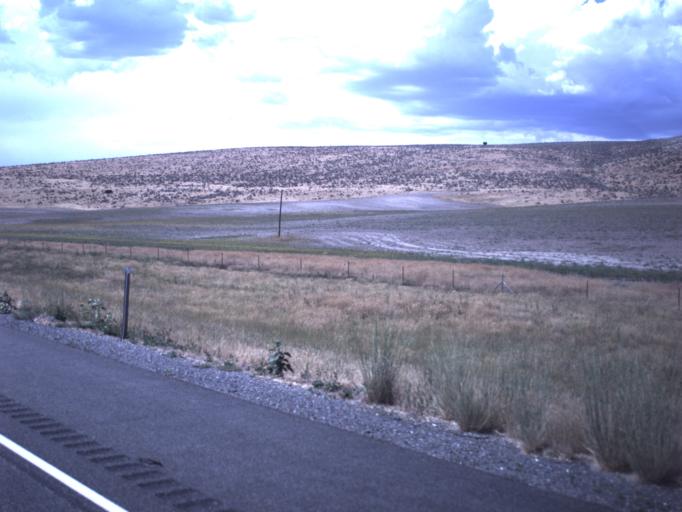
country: US
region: Idaho
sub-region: Oneida County
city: Malad City
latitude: 41.9149
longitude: -112.6171
